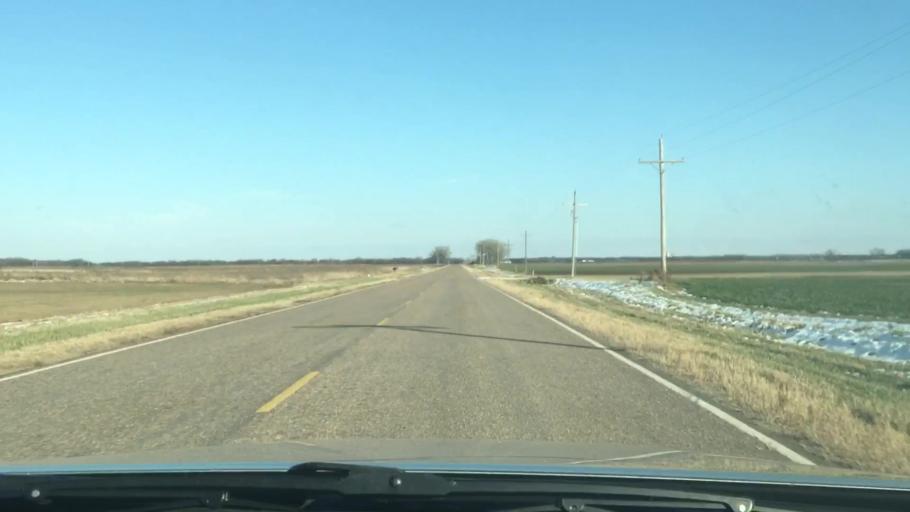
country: US
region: Kansas
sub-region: Rice County
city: Lyons
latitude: 38.2895
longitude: -98.1752
